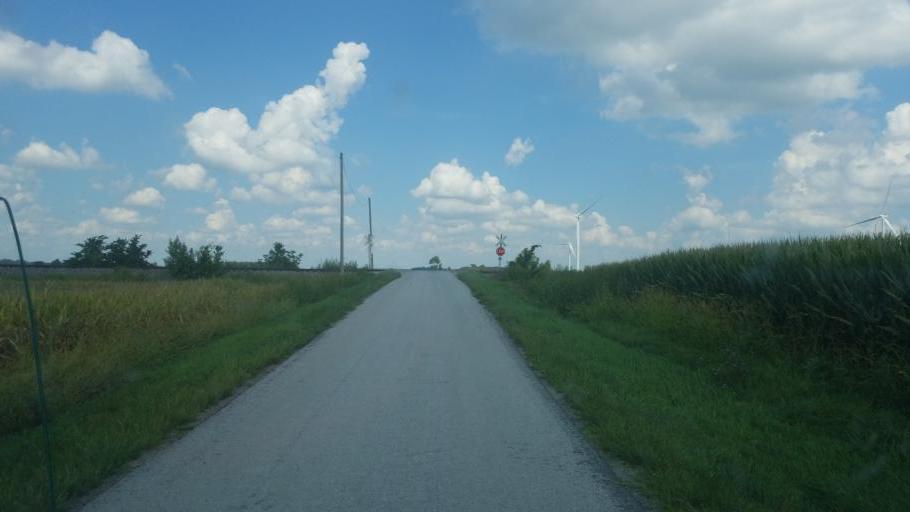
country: US
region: Ohio
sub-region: Hardin County
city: Ada
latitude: 40.7777
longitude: -83.7479
